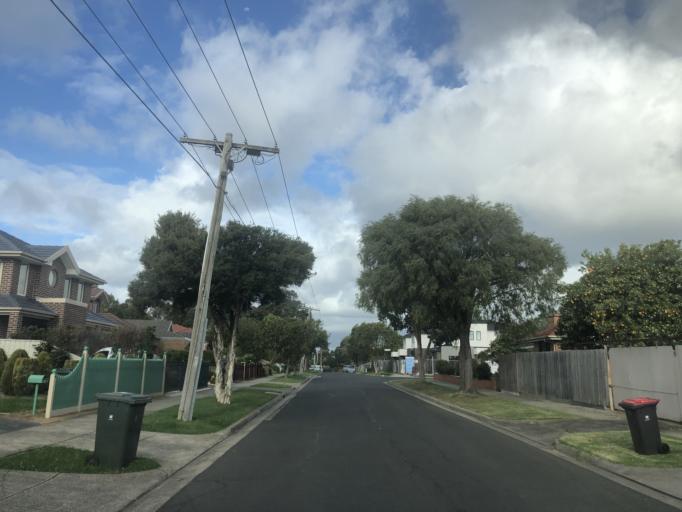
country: AU
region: Victoria
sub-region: Monash
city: Ashwood
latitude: -37.8792
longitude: 145.1123
